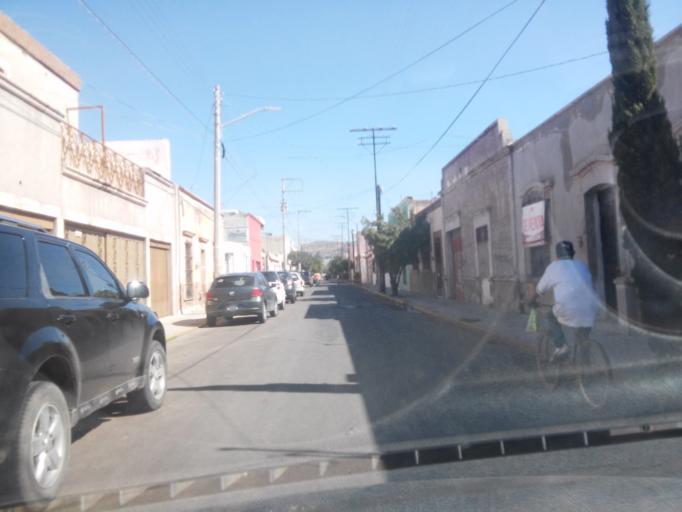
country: MX
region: Durango
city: Victoria de Durango
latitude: 24.0303
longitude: -104.6693
